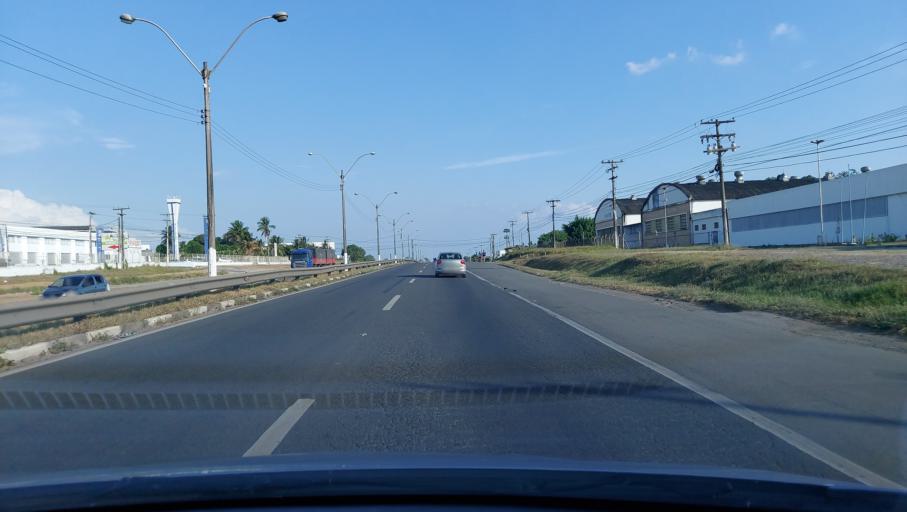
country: BR
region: Bahia
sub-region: Feira De Santana
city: Feira de Santana
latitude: -12.2810
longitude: -38.9241
